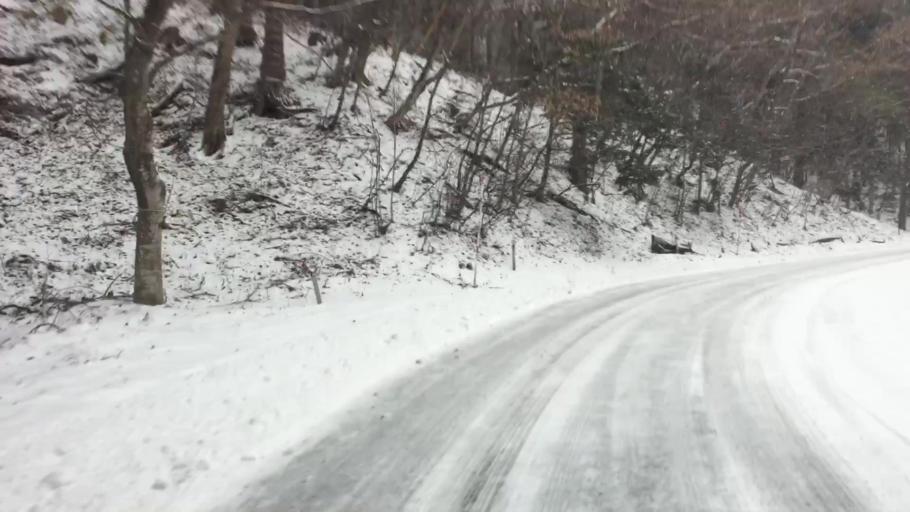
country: JP
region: Tochigi
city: Nikko
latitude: 36.8747
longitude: 139.7201
